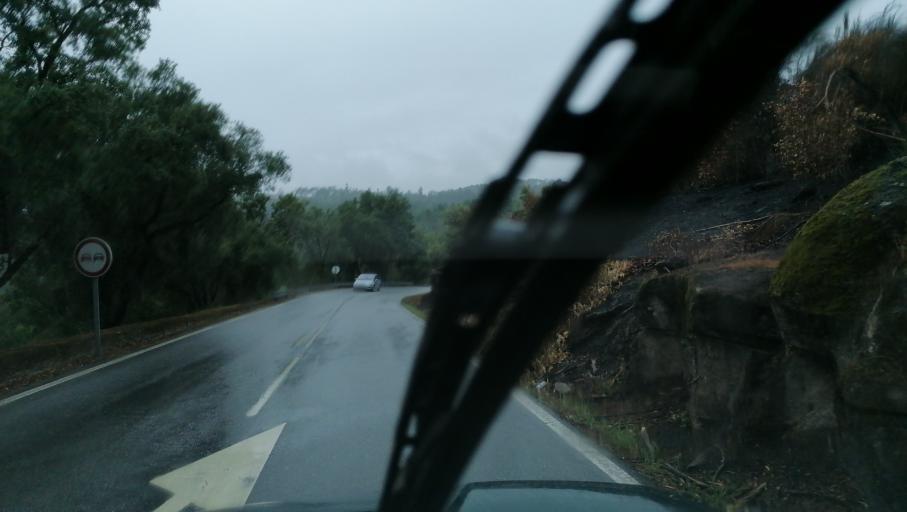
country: PT
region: Braga
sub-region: Cabeceiras de Basto
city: Cabeceiras de Basto
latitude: 41.4921
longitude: -7.9389
